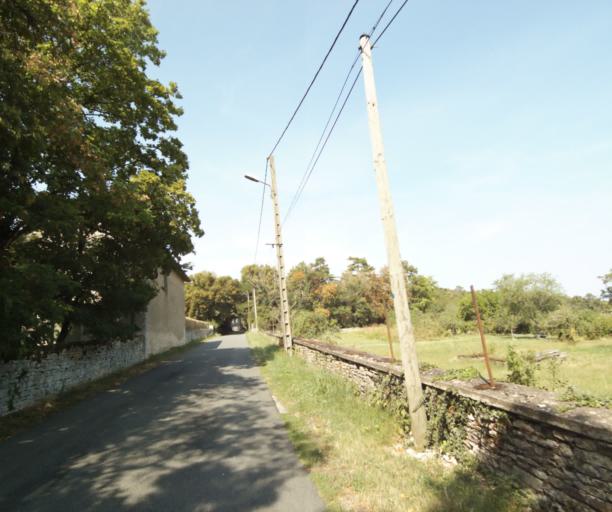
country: FR
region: Bourgogne
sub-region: Departement de Saone-et-Loire
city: Tournus
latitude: 46.5755
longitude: 4.8902
